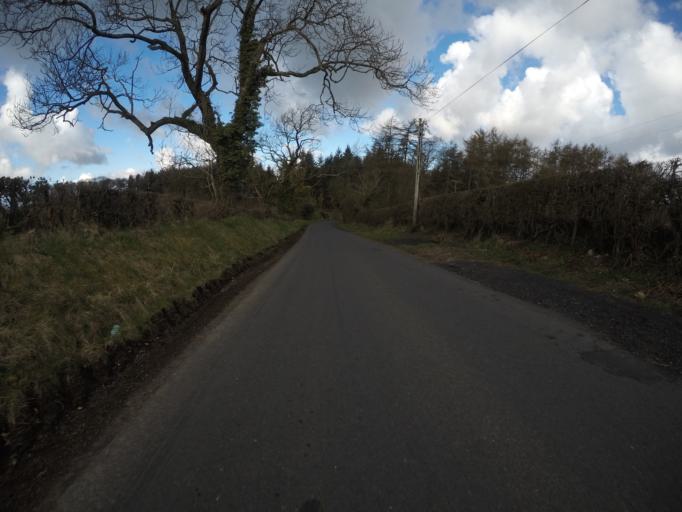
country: GB
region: Scotland
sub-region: North Ayrshire
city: Kilwinning
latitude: 55.6910
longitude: -4.6724
